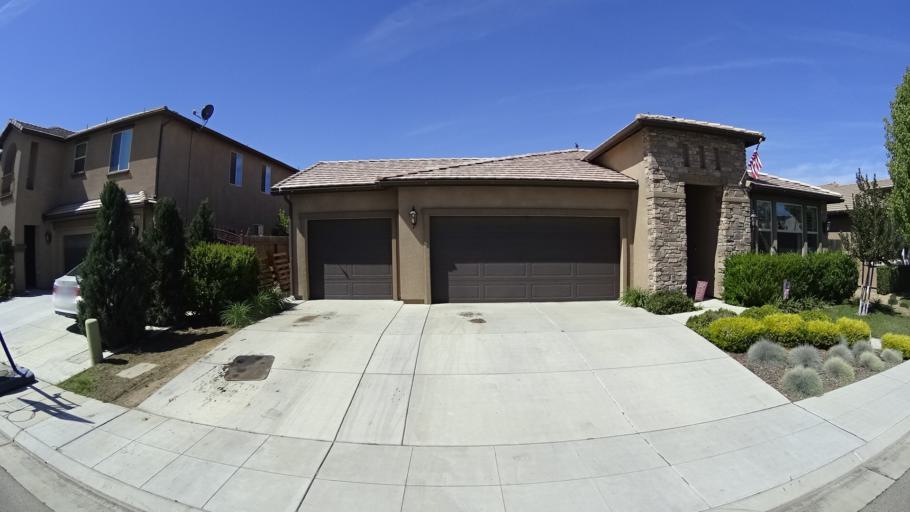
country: US
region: California
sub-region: Fresno County
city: Biola
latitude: 36.8173
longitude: -119.9240
